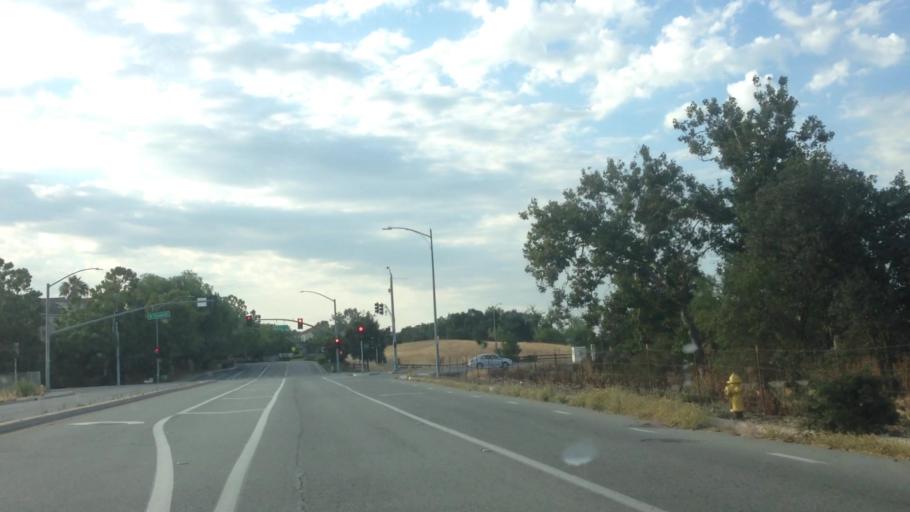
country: US
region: California
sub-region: Santa Clara County
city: Seven Trees
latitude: 37.2508
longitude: -121.7716
